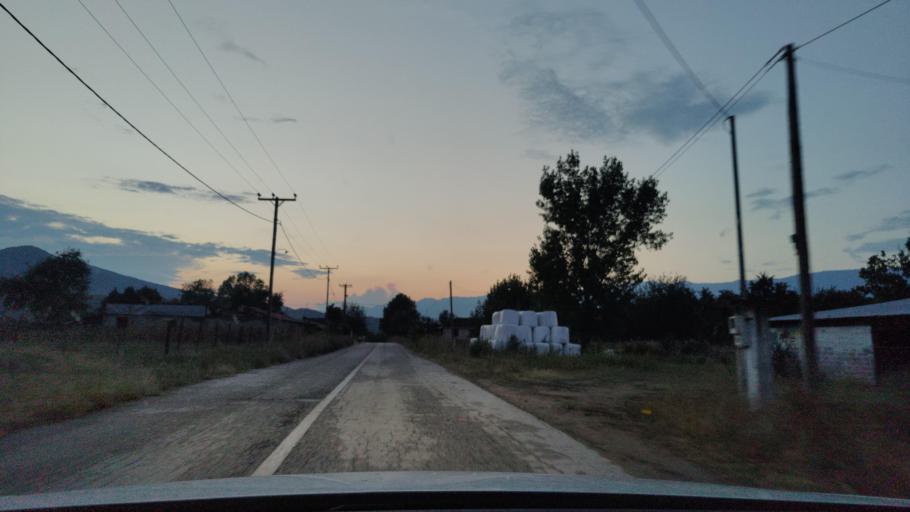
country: GR
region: Central Macedonia
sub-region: Nomos Serron
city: Chrysochorafa
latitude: 41.1807
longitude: 23.1085
